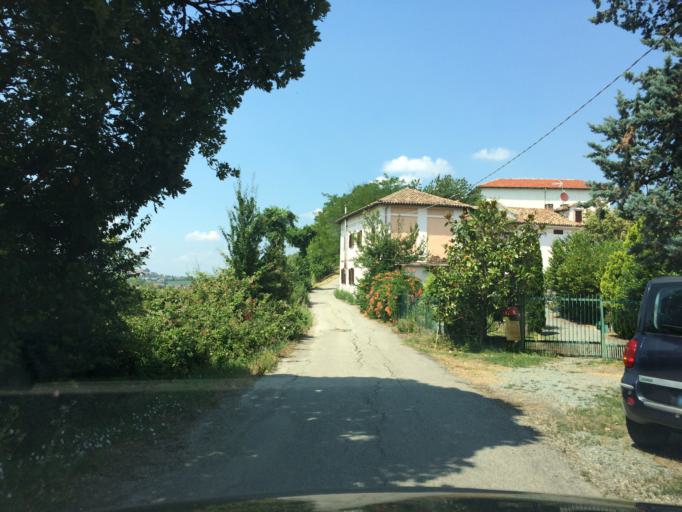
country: IT
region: Piedmont
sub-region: Provincia di Asti
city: Moasca
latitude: 44.7603
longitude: 8.2604
